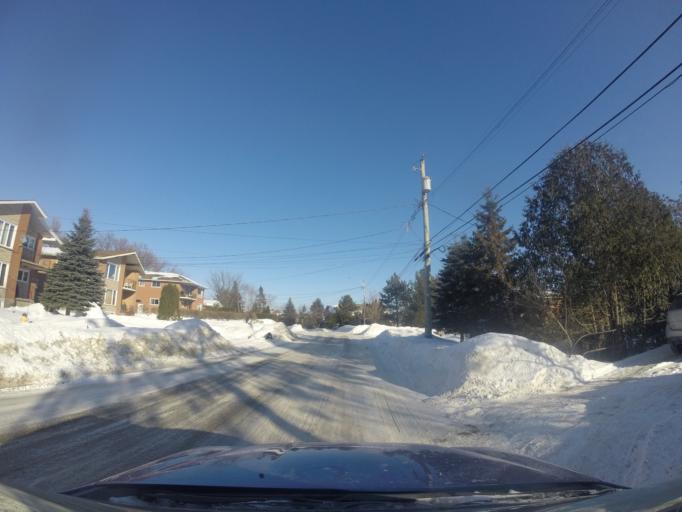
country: CA
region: Ontario
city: Greater Sudbury
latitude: 46.4624
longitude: -80.9933
